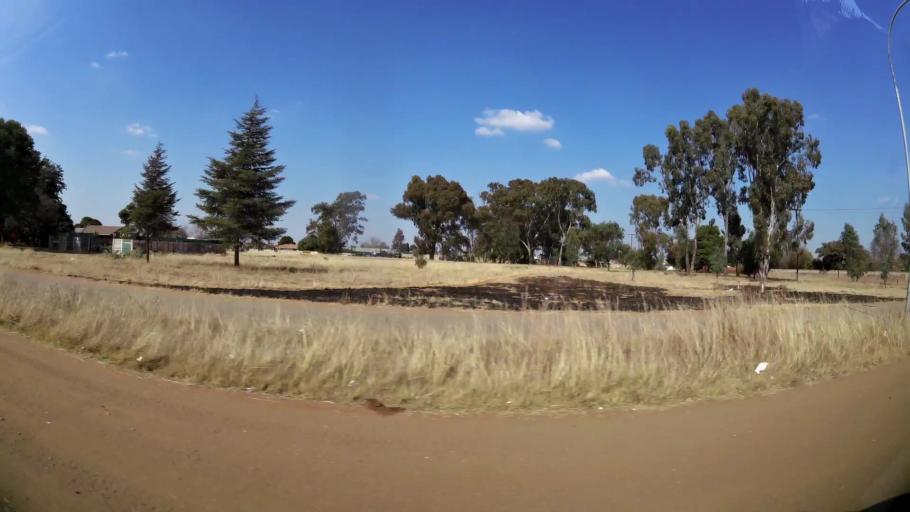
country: ZA
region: Gauteng
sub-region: Ekurhuleni Metropolitan Municipality
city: Benoni
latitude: -26.1183
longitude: 28.4044
